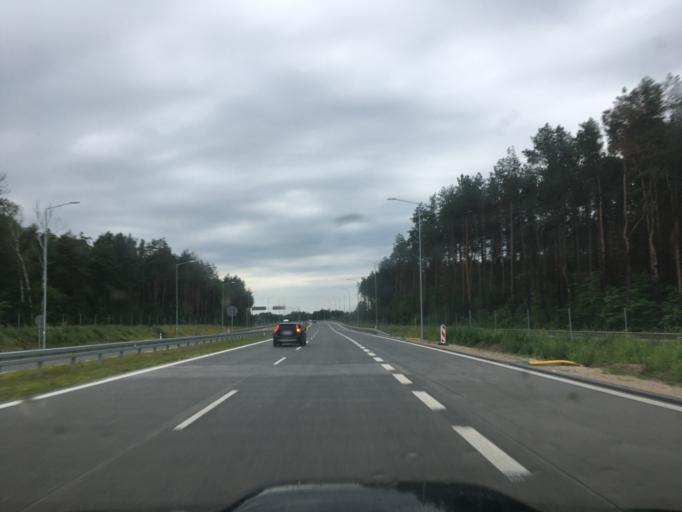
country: PL
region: Masovian Voivodeship
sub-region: Powiat piaseczynski
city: Gora Kalwaria
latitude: 51.9730
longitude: 21.1925
